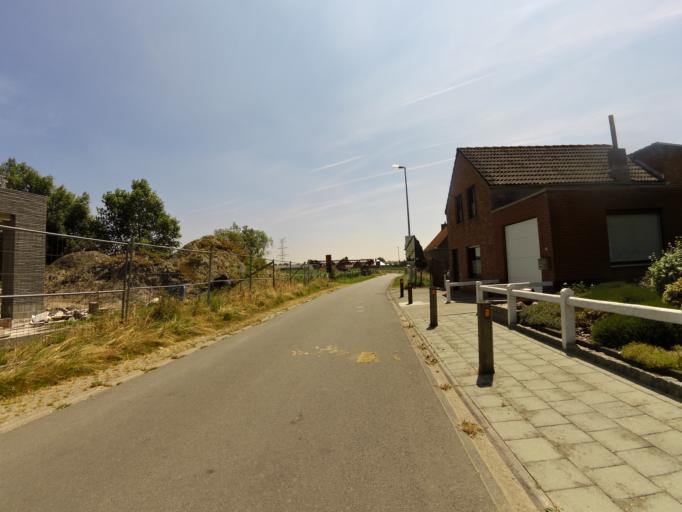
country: BE
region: Flanders
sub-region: Provincie West-Vlaanderen
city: Zedelgem
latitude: 51.1675
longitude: 3.1256
